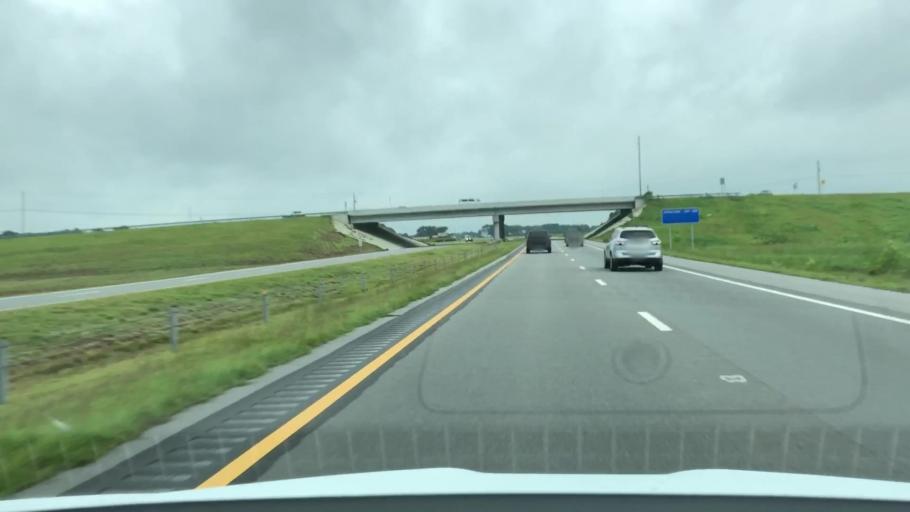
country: US
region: North Carolina
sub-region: Wayne County
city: Elroy
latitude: 35.4114
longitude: -77.8957
